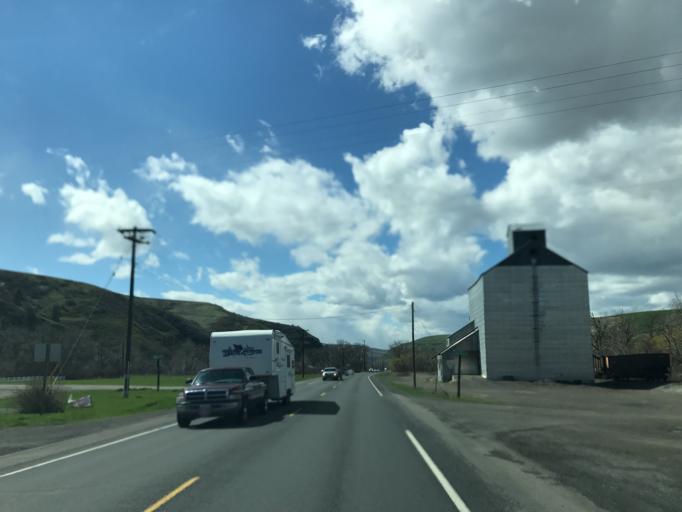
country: US
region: Idaho
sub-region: Nez Perce County
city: Lapwai
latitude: 46.3698
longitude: -116.7245
